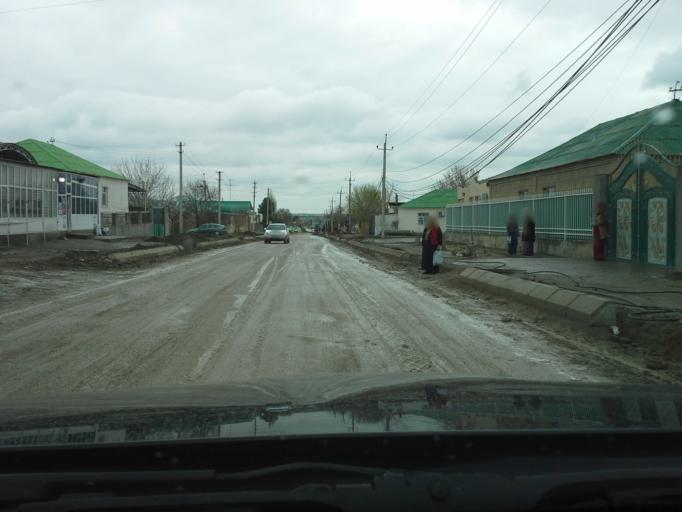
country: TM
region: Ahal
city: Abadan
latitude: 37.9642
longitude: 58.2136
